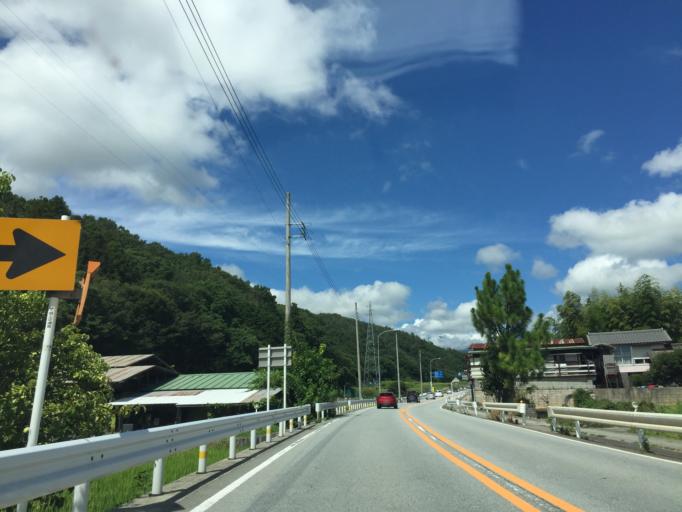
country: JP
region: Yamanashi
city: Nirasaki
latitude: 35.7966
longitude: 138.3622
